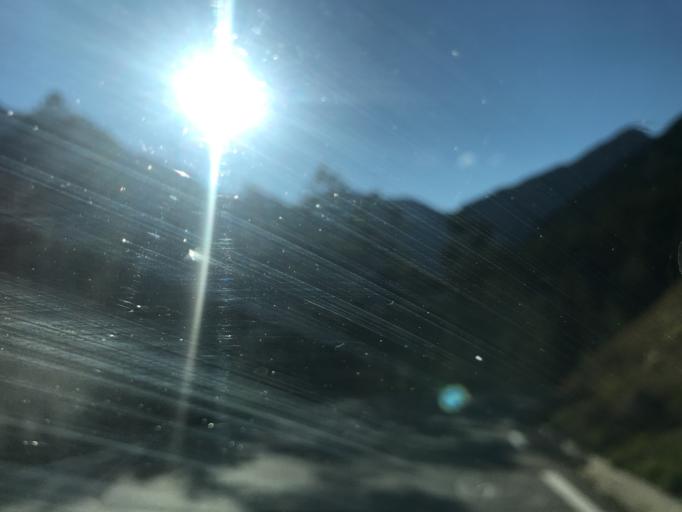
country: FR
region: Provence-Alpes-Cote d'Azur
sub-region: Departement des Hautes-Alpes
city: Villar-Saint-Pancrace
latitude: 44.7960
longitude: 6.7322
